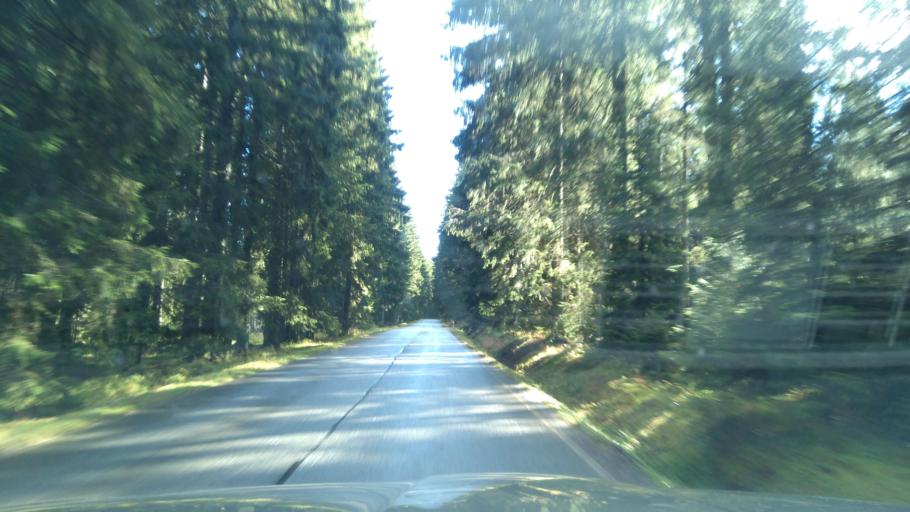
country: CZ
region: Jihocesky
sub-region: Okres Prachatice
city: Borova Lada
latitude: 49.0256
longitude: 13.5531
